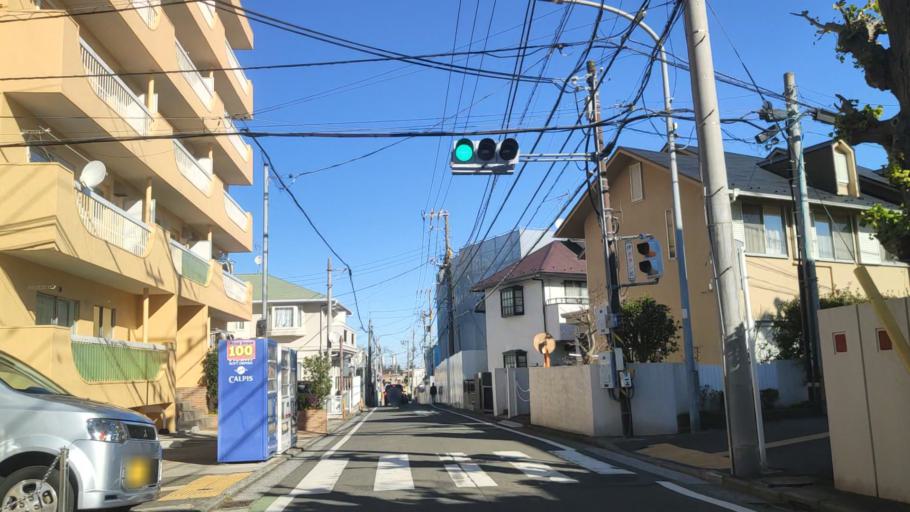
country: JP
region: Kanagawa
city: Yokohama
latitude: 35.4291
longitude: 139.6438
